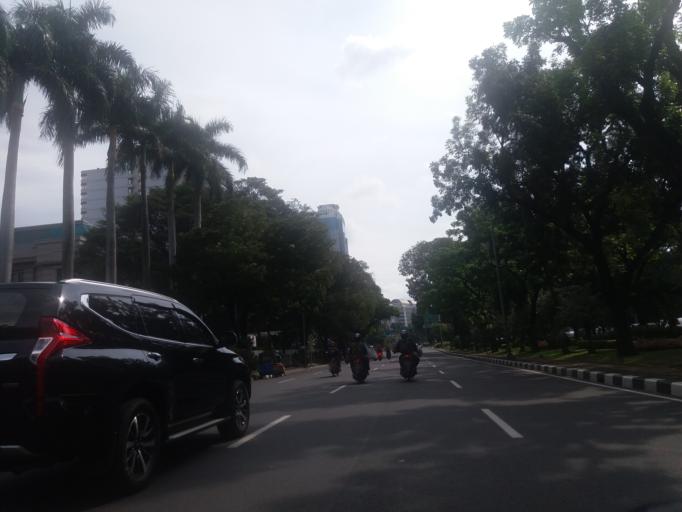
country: ID
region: Jakarta Raya
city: Jakarta
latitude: -6.1806
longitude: 106.8258
